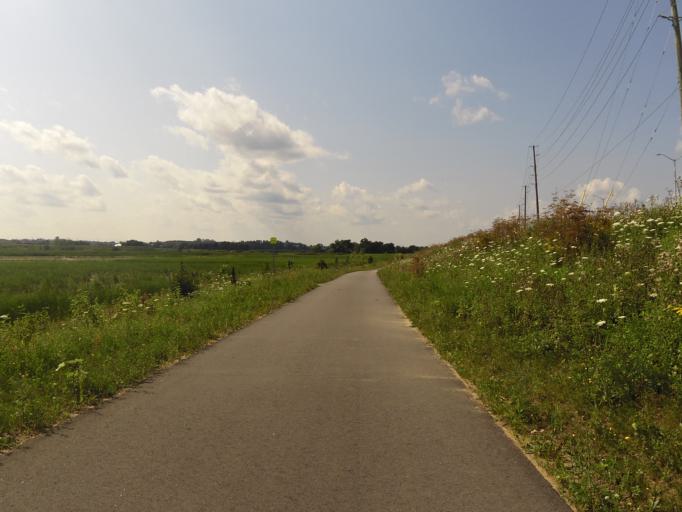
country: CA
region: Ontario
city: Bells Corners
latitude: 45.3094
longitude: -75.9280
